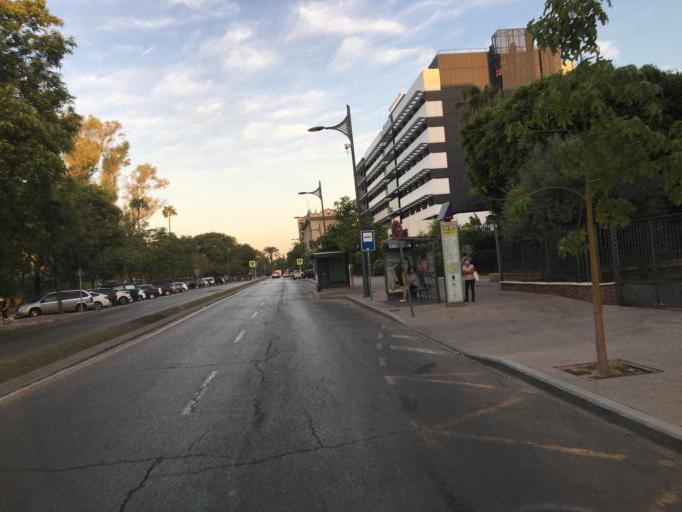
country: ES
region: Murcia
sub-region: Murcia
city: Murcia
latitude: 37.9817
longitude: -1.1232
